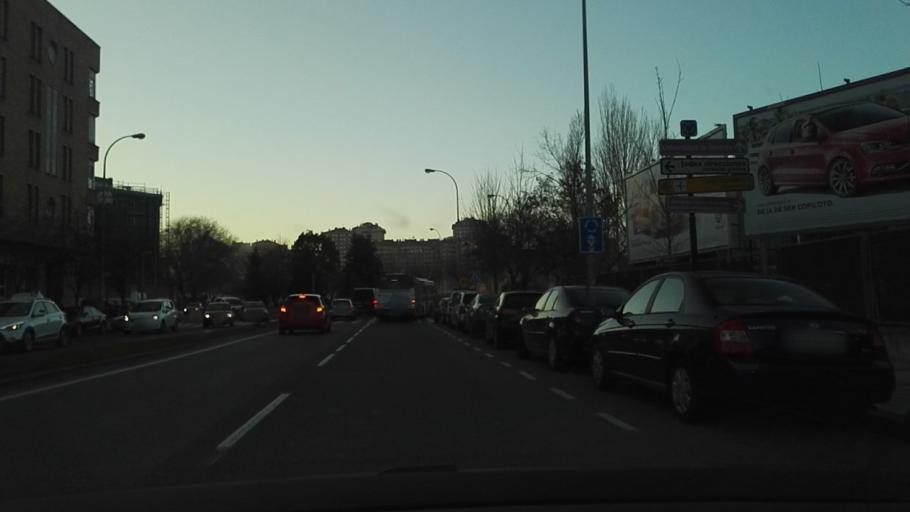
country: ES
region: Navarre
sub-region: Provincia de Navarra
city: Segundo Ensanche
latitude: 42.7985
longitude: -1.6396
